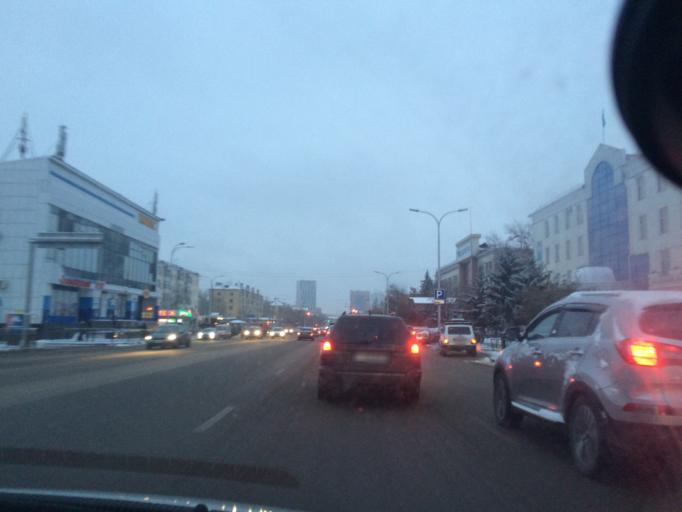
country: KZ
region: Astana Qalasy
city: Astana
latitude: 51.1783
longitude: 71.4174
